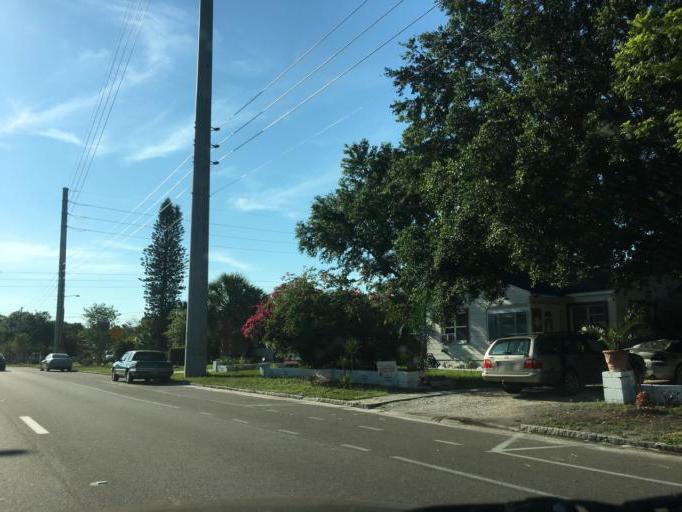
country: US
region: Florida
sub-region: Pinellas County
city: Saint Petersburg
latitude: 27.7700
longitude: -82.6819
